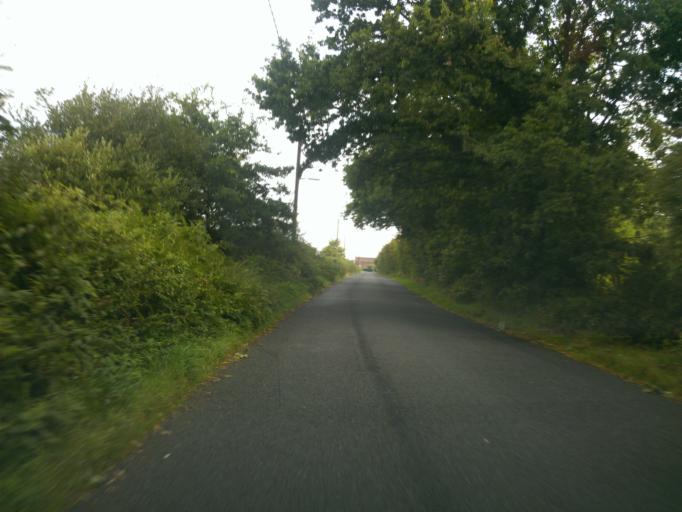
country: GB
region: England
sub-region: Essex
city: Saint Osyth
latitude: 51.8208
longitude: 1.0987
